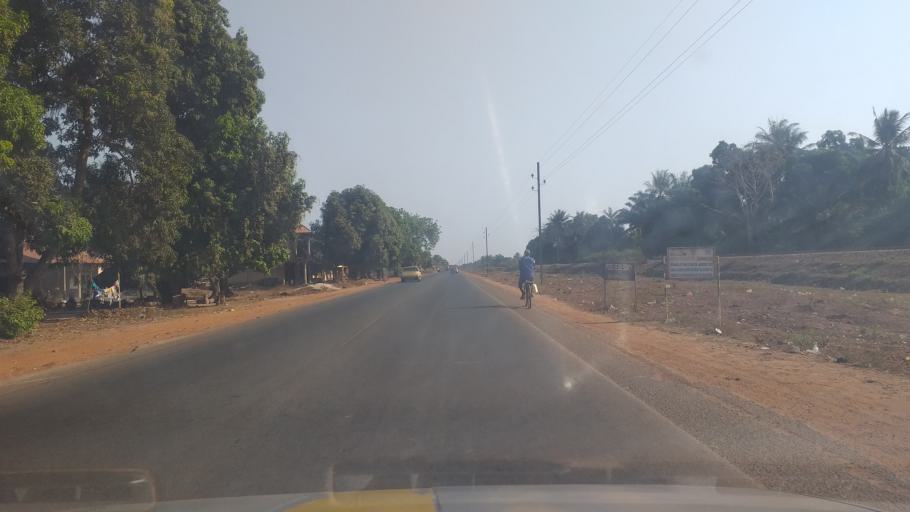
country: GN
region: Boke
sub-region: Boke Prefecture
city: Kamsar
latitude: 10.7167
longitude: -14.5217
